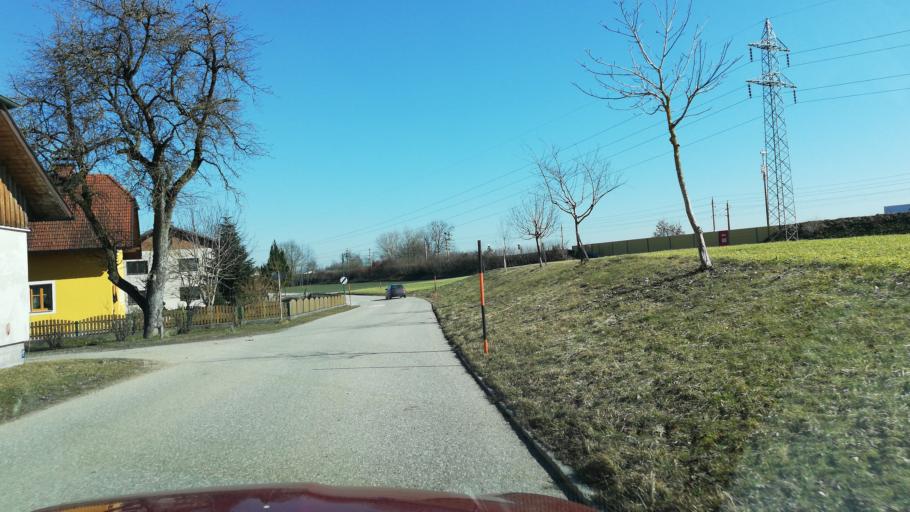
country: AT
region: Upper Austria
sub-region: Politischer Bezirk Vocklabruck
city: Redlham
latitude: 48.0347
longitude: 13.7398
